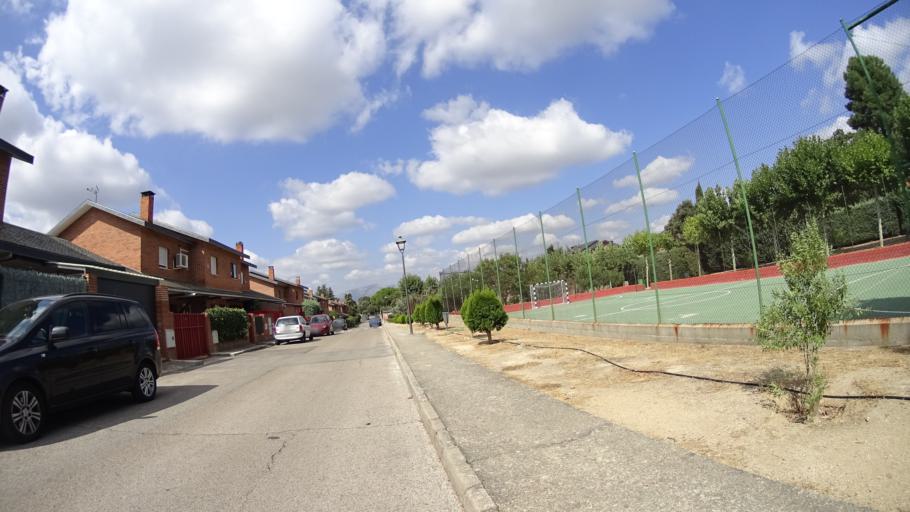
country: ES
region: Madrid
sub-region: Provincia de Madrid
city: Galapagar
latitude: 40.5836
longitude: -3.9883
